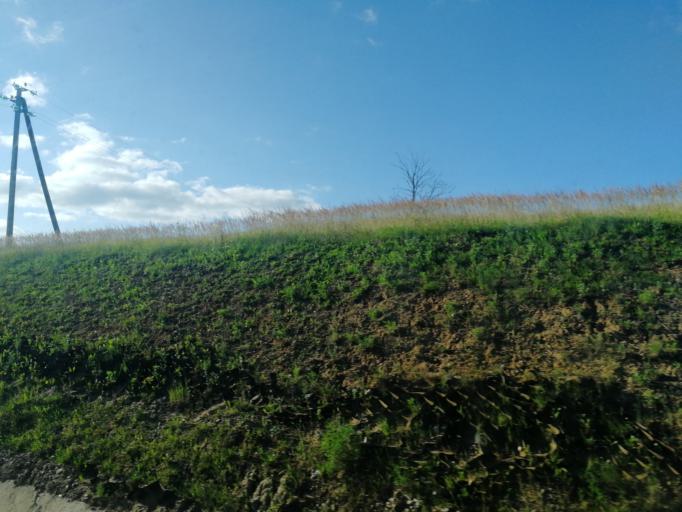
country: RU
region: Tula
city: Dubna
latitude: 54.2817
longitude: 37.1667
